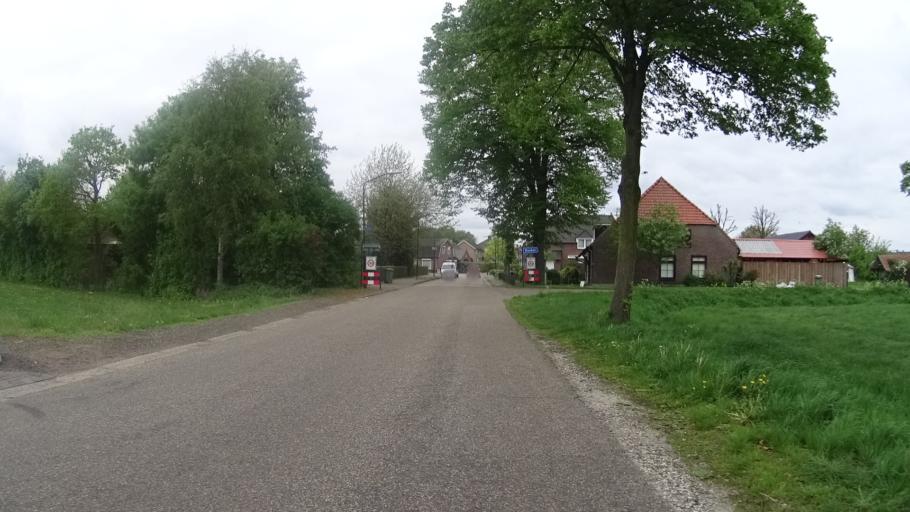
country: NL
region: North Brabant
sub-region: Gemeente Boekel
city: Boekel
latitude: 51.6079
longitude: 5.6794
